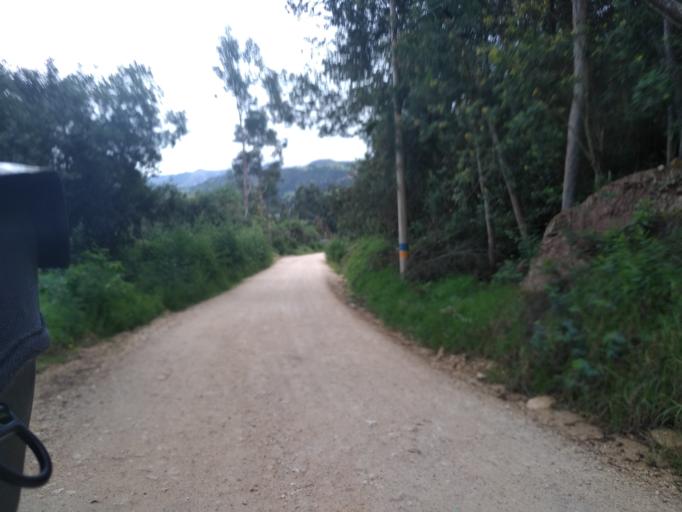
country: CO
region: Cundinamarca
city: Lenguazaque
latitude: 5.2919
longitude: -73.7214
